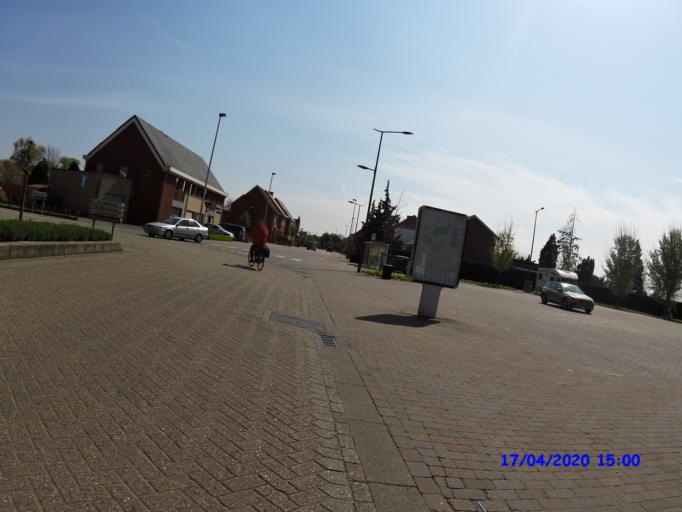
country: BE
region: Flanders
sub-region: Provincie Antwerpen
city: Oud-Turnhout
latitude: 51.3364
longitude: 4.9732
